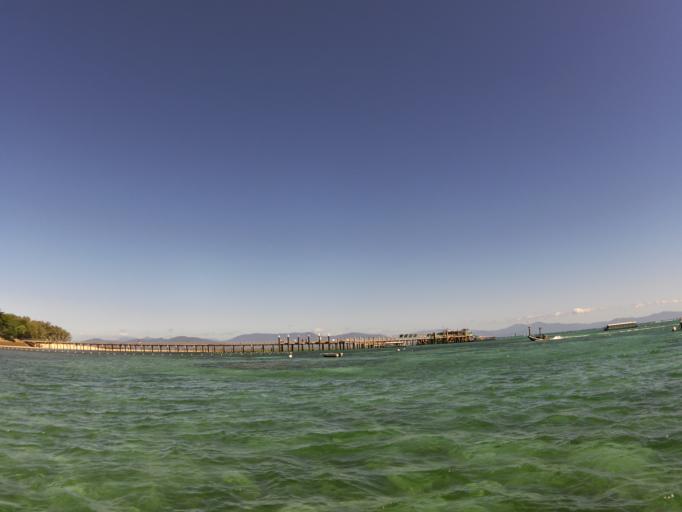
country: AU
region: Queensland
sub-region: Cairns
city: Yorkeys Knob
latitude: -16.7564
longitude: 145.9714
